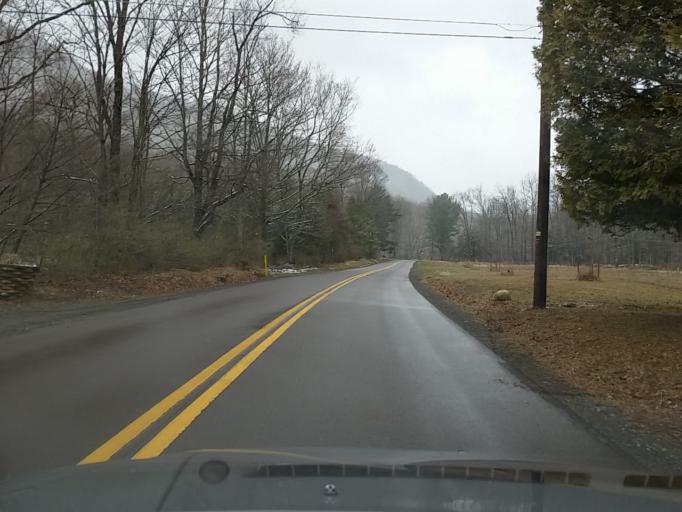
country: US
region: Pennsylvania
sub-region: Sullivan County
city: Laporte
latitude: 41.2998
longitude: -76.3846
